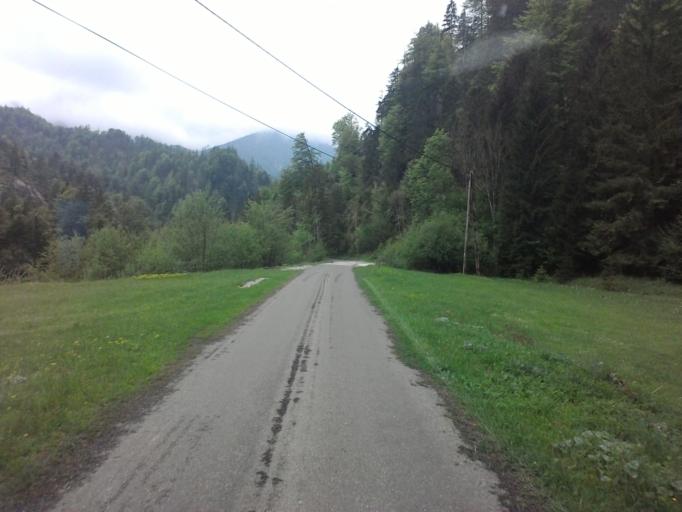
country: AT
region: Styria
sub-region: Politischer Bezirk Liezen
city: Wildalpen
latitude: 47.6964
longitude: 14.9479
